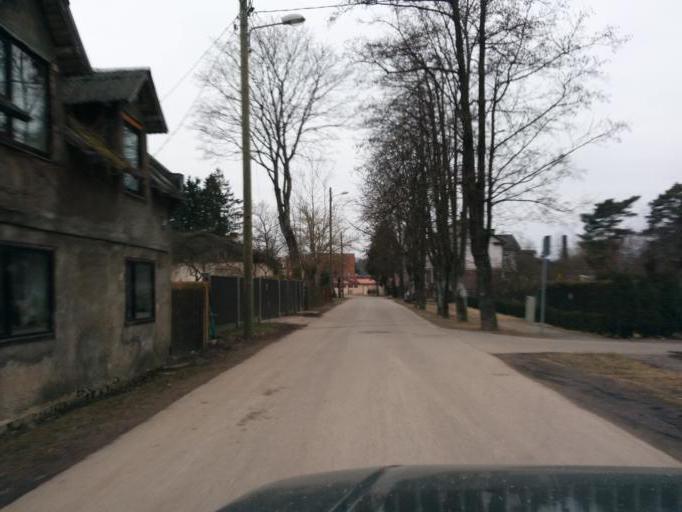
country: LV
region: Jurmala
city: Jurmala
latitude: 56.9654
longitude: 23.8282
